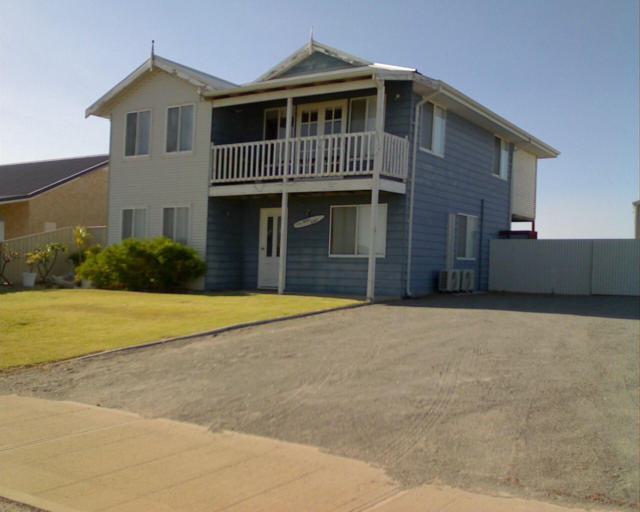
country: AU
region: Western Australia
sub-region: Dandaragan
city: Jurien Bay
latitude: -30.0698
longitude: 114.9766
